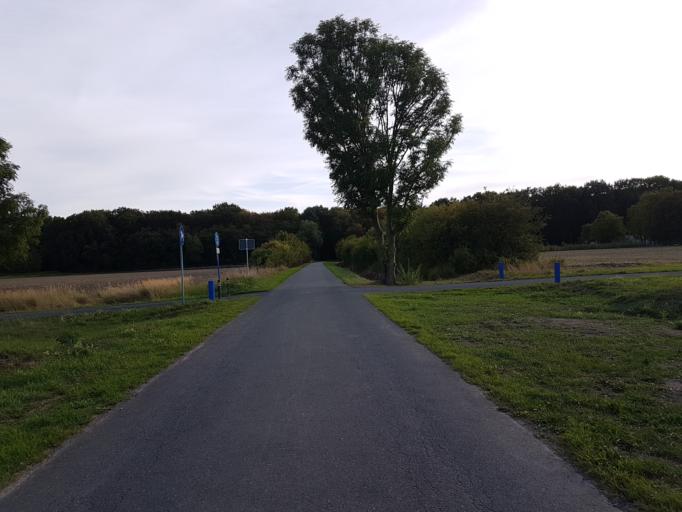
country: DE
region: Lower Saxony
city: Laatzen
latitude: 52.3486
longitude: 9.8684
